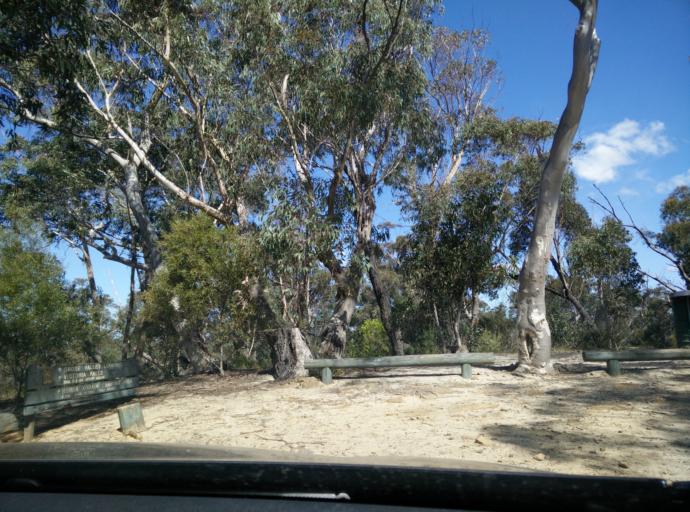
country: AU
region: New South Wales
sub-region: Blue Mountains Municipality
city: Blackheath
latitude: -33.5737
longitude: 150.2921
